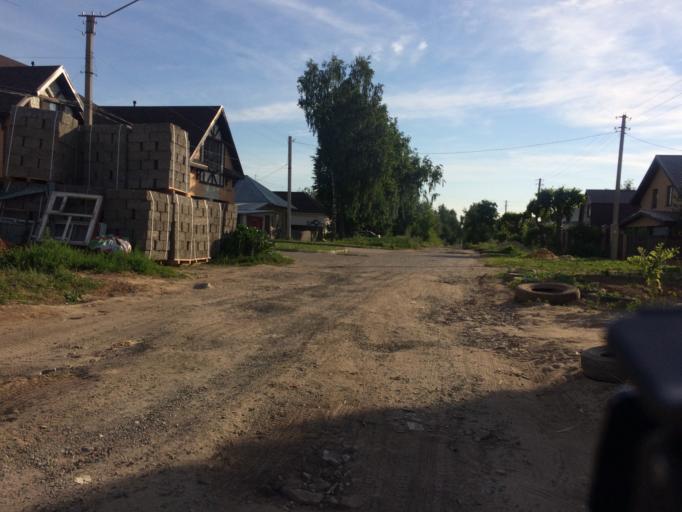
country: RU
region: Mariy-El
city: Yoshkar-Ola
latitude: 56.6476
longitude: 47.9134
